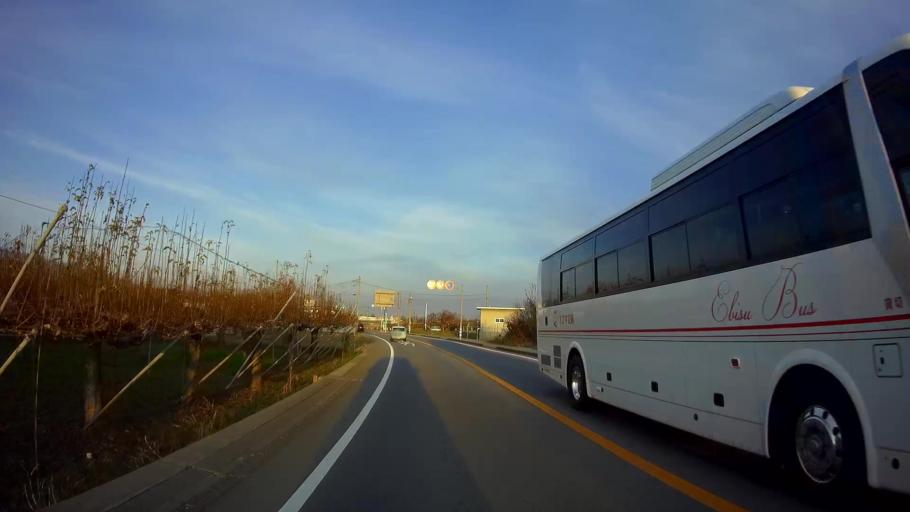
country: JP
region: Yamanashi
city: Kofu-shi
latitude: 35.5965
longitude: 138.5770
